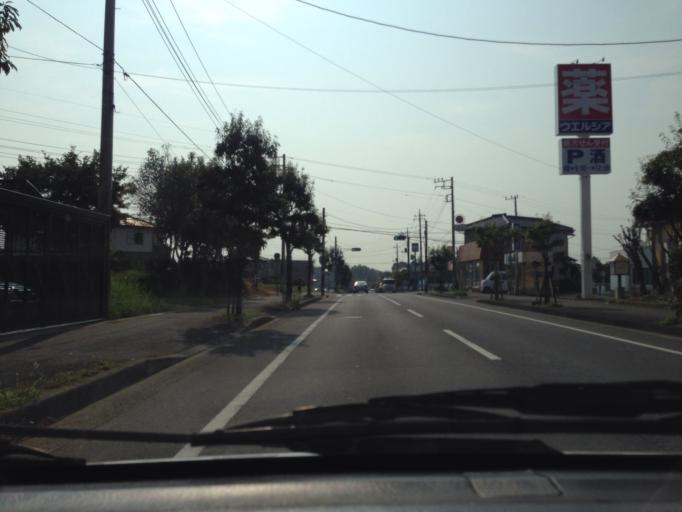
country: JP
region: Ibaraki
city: Ami
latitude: 36.0605
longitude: 140.2022
